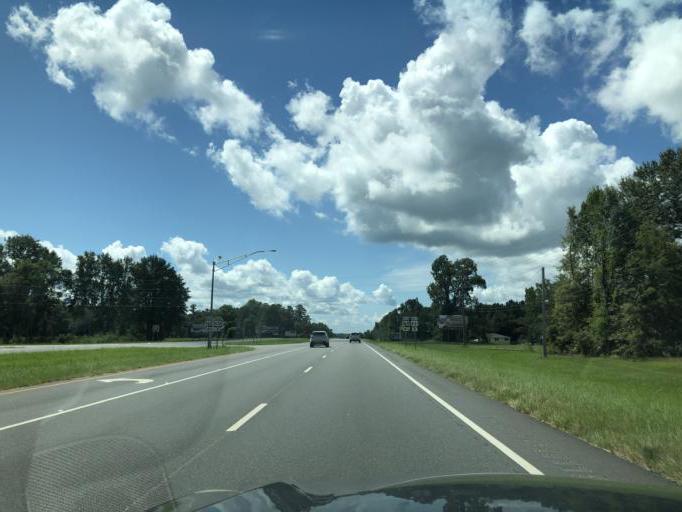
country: US
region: Alabama
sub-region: Barbour County
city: Eufaula
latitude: 32.0012
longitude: -85.1160
